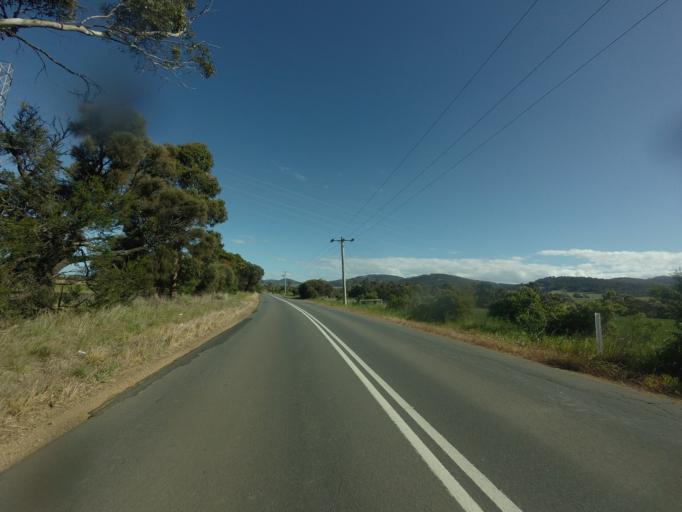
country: AU
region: Tasmania
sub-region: Clarence
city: Cambridge
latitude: -42.7645
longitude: 147.4149
